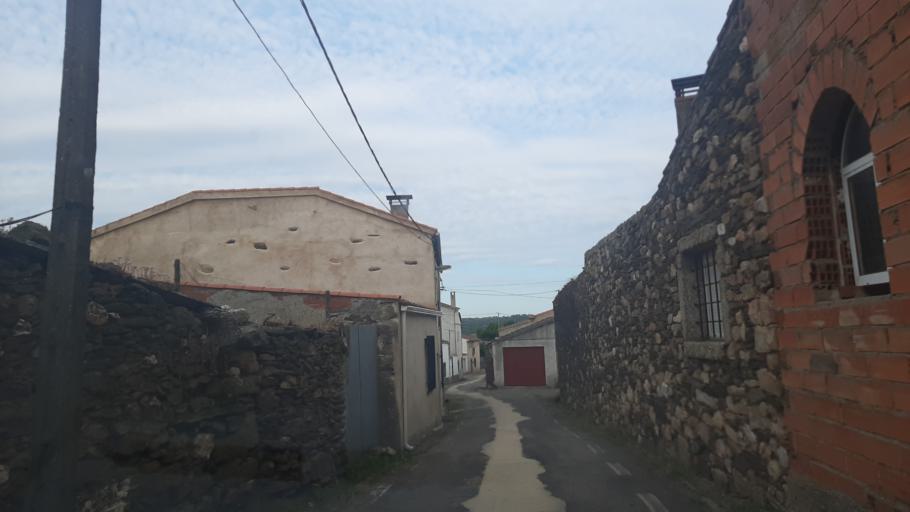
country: ES
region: Castille and Leon
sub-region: Provincia de Salamanca
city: Gallegos de Arganan
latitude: 40.6511
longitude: -6.7593
